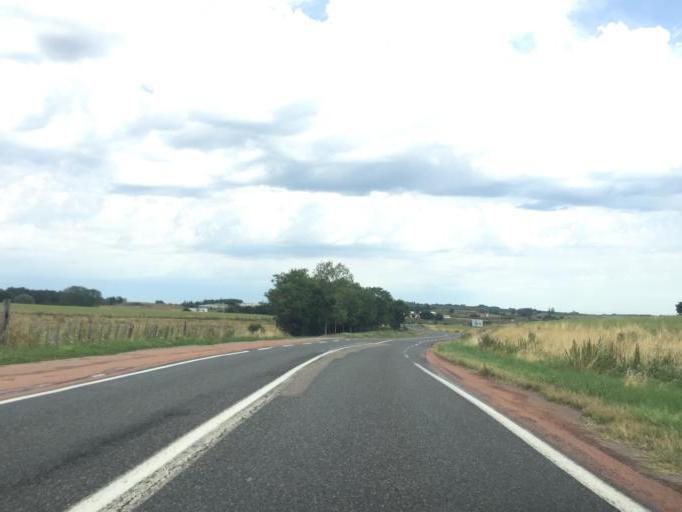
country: FR
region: Rhone-Alpes
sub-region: Departement du Rhone
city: Saint-Romain-de-Popey
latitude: 45.8775
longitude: 4.5298
